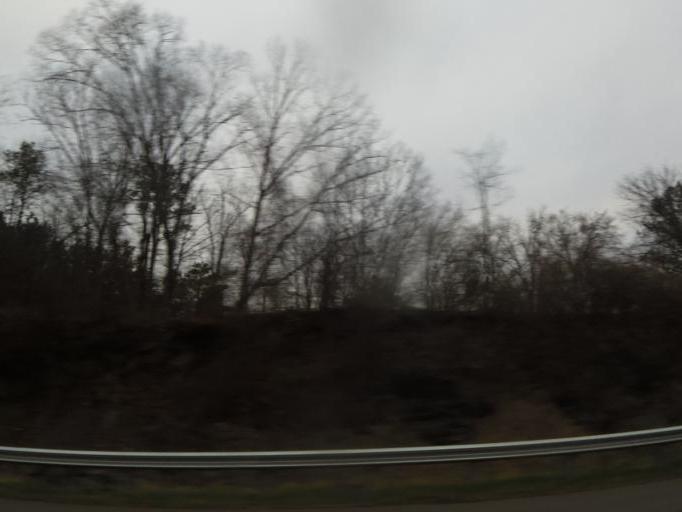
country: US
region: Alabama
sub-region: Jefferson County
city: Warrior
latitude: 33.8296
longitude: -86.8243
